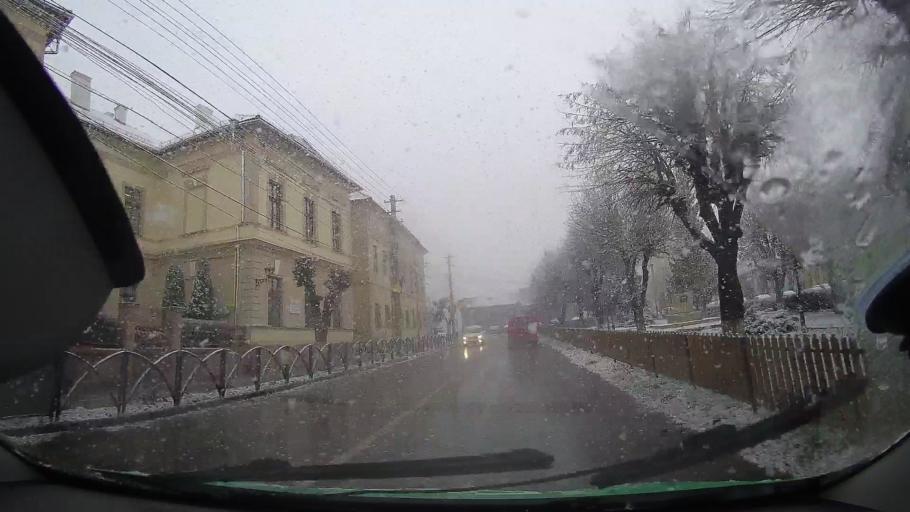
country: RO
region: Sibiu
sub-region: Municipiul Medias
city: Medias
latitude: 46.1669
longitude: 24.3538
